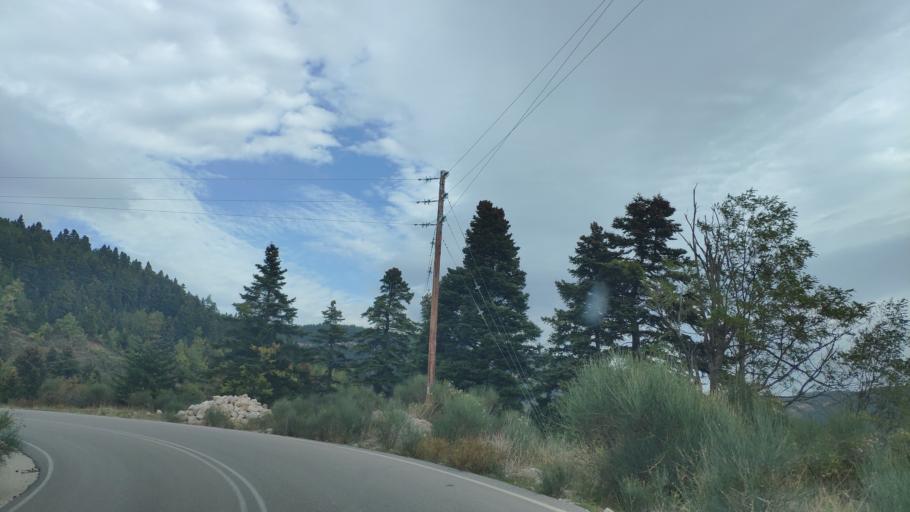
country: GR
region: Central Greece
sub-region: Nomos Fokidos
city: Amfissa
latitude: 38.6898
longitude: 22.3205
